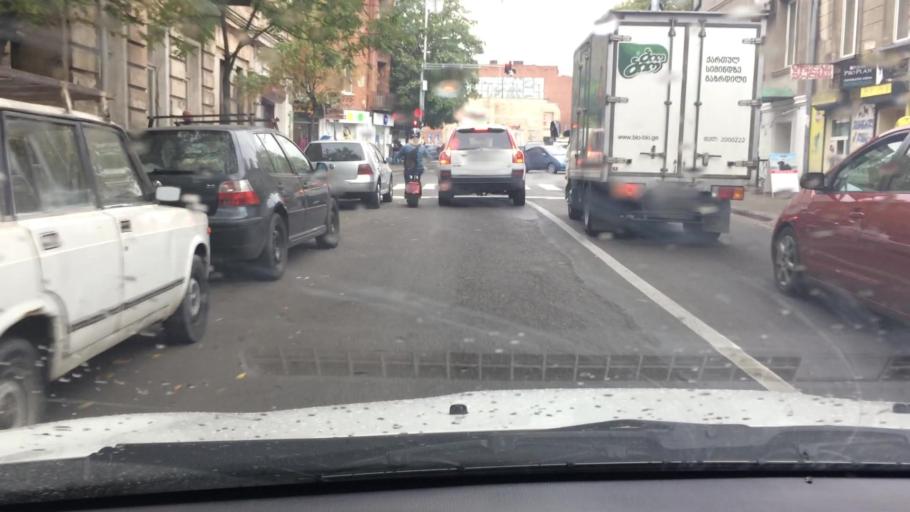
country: GE
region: T'bilisi
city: Tbilisi
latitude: 41.7096
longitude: 44.8042
